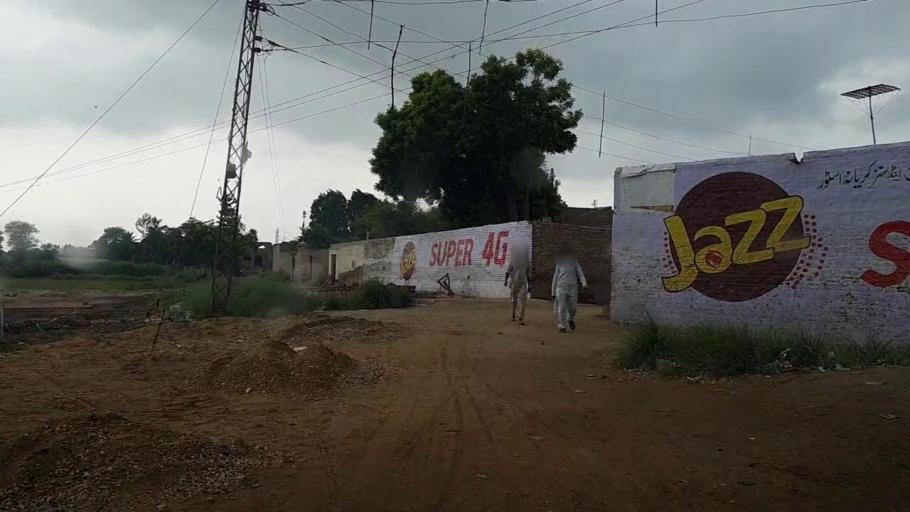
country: PK
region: Sindh
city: Naushahro Firoz
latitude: 26.8698
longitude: 68.1517
